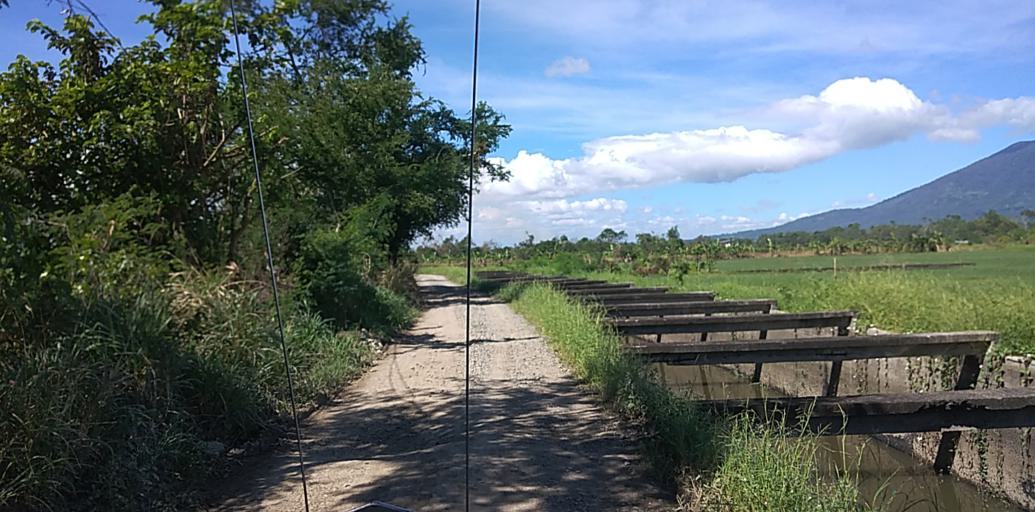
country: PH
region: Central Luzon
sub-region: Province of Pampanga
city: Arayat
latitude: 15.1289
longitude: 120.7888
